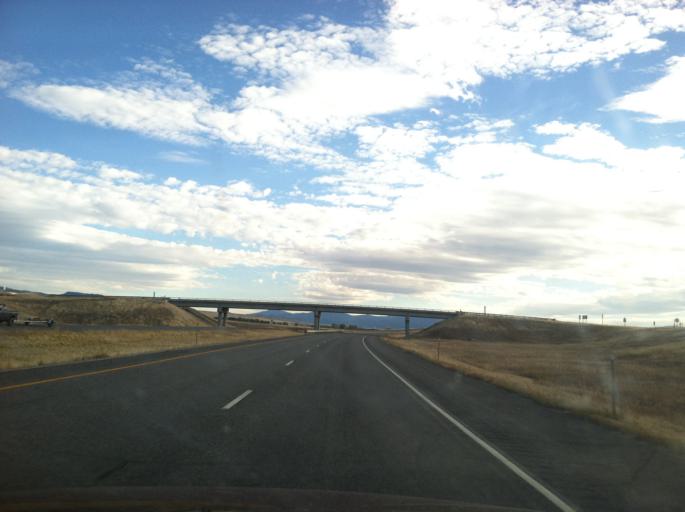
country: US
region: Montana
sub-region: Deer Lodge County
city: Warm Springs
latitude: 46.2721
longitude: -112.7478
